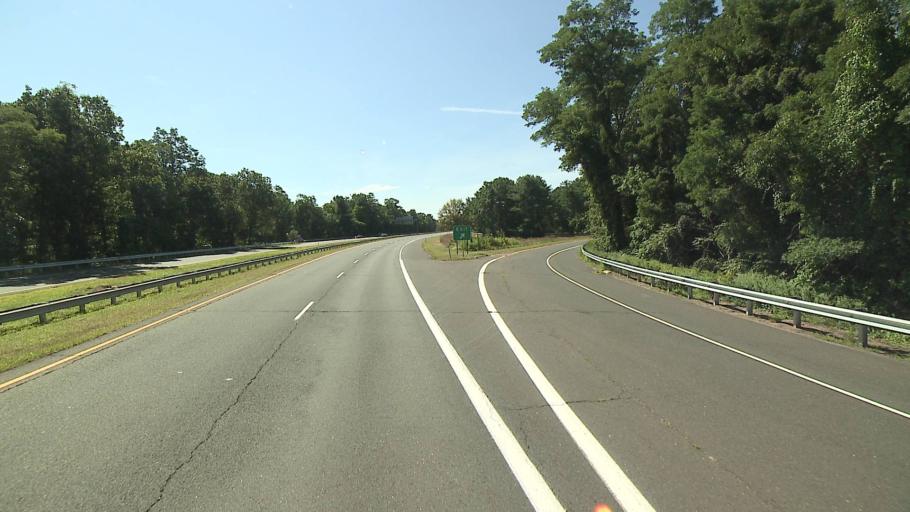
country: US
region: Connecticut
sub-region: Hartford County
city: Tariffville
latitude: 41.8912
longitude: -72.7494
